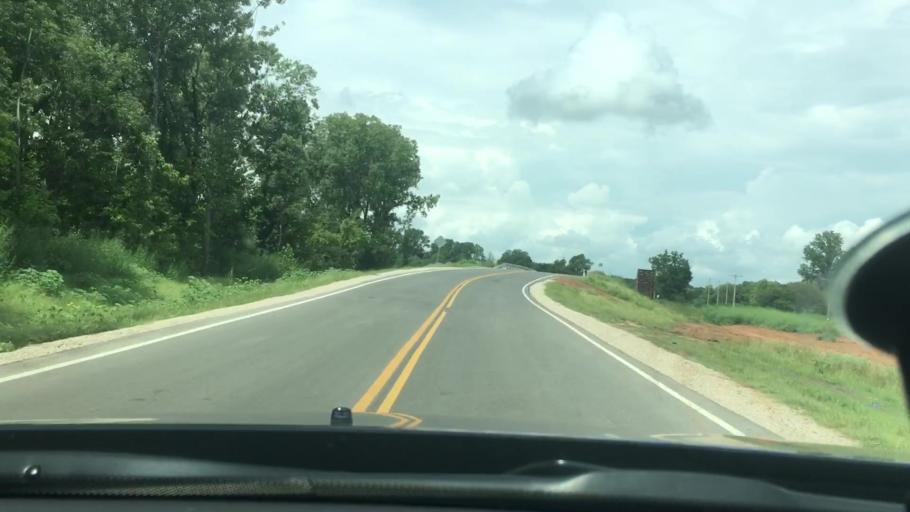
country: US
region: Oklahoma
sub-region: Carter County
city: Dickson
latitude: 34.2280
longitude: -96.9056
